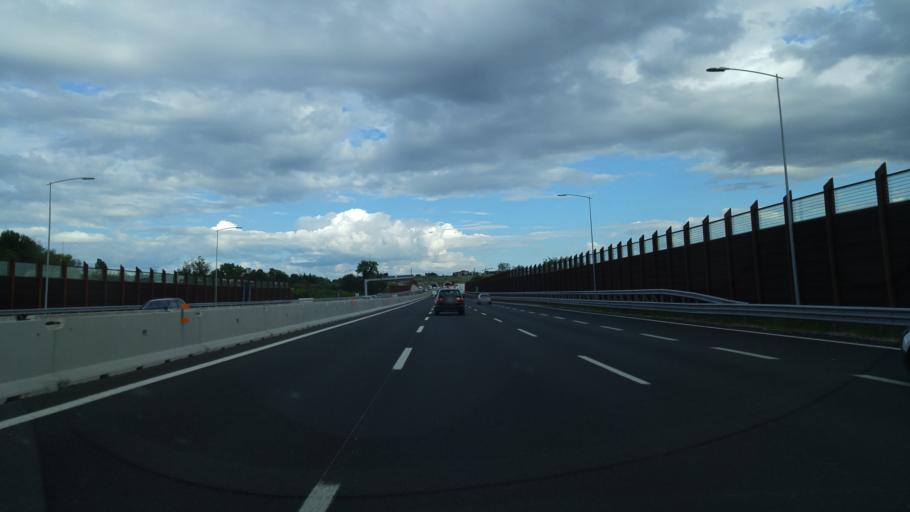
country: IT
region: Emilia-Romagna
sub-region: Provincia di Rimini
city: Riccione
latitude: 43.9850
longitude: 12.6409
